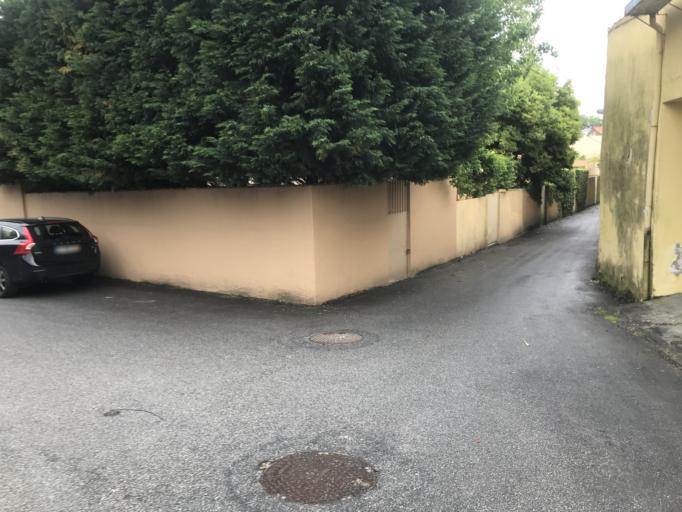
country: PT
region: Porto
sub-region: Matosinhos
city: Senhora da Hora
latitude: 41.1811
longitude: -8.6607
